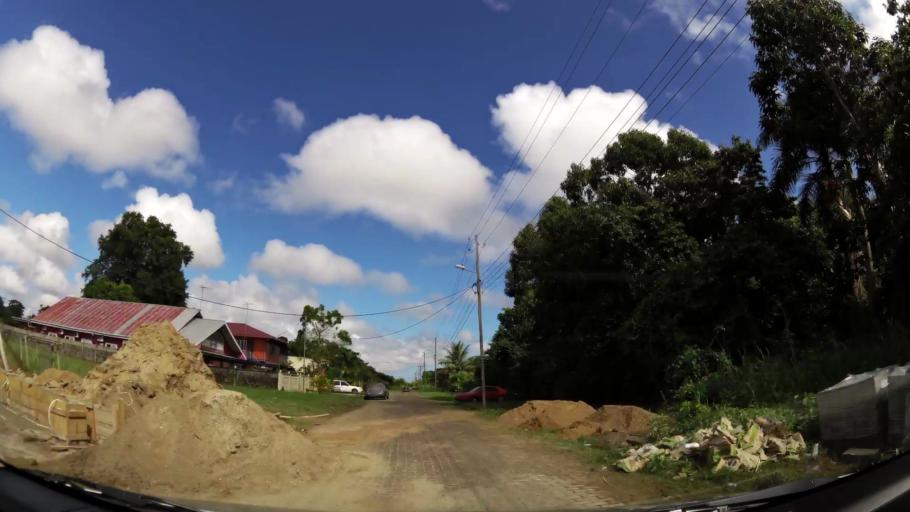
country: SR
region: Commewijne
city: Nieuw Amsterdam
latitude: 5.8760
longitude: -55.1087
